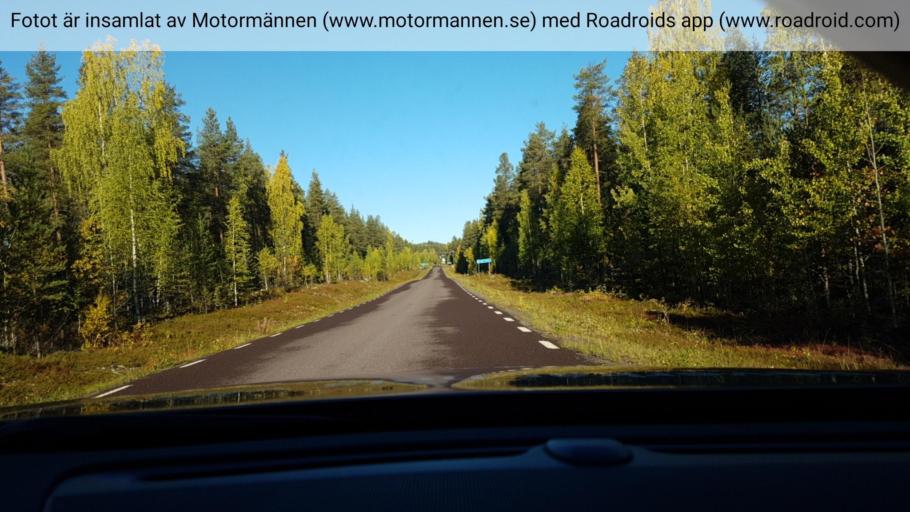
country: SE
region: Norrbotten
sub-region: Bodens Kommun
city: Boden
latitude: 66.1169
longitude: 21.3384
